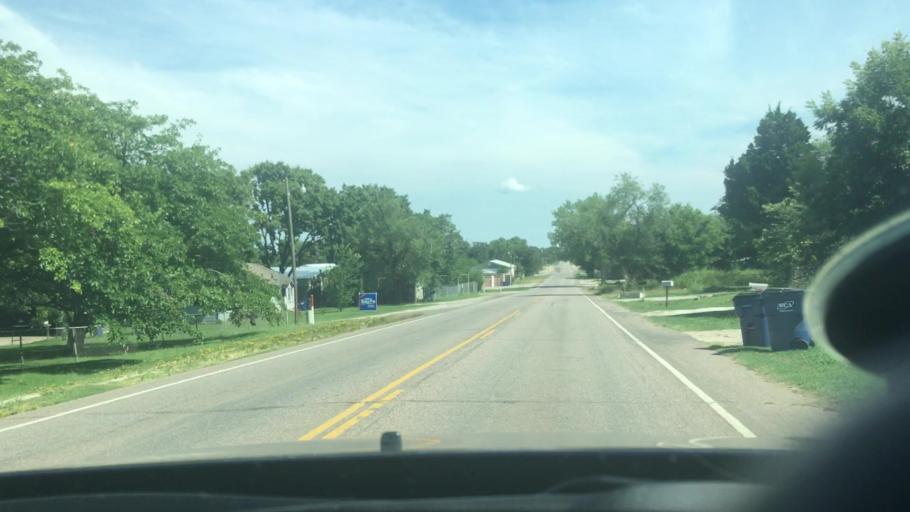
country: US
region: Oklahoma
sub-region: Seminole County
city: Seminole
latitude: 35.2366
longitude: -96.6916
